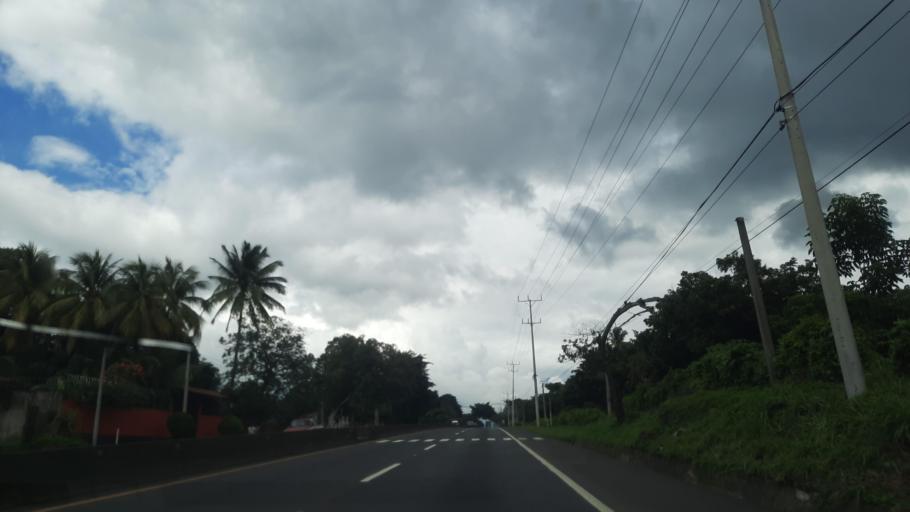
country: SV
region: Sonsonate
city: Izalco
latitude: 13.7447
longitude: -89.6398
